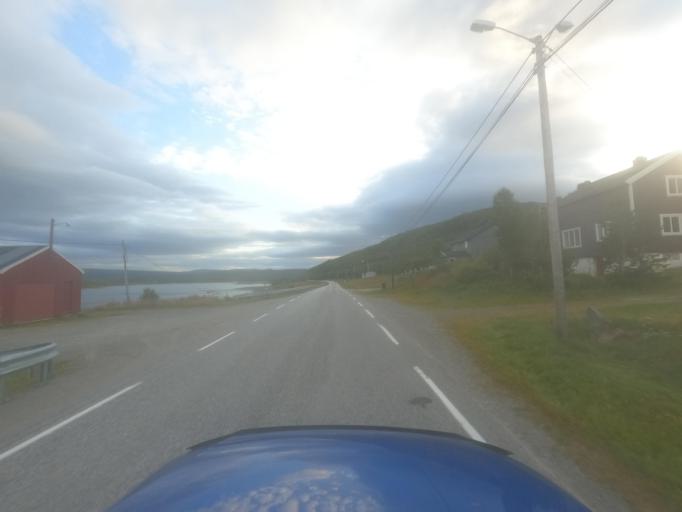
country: NO
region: Finnmark Fylke
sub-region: Porsanger
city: Lakselv
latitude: 70.5168
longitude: 25.0737
